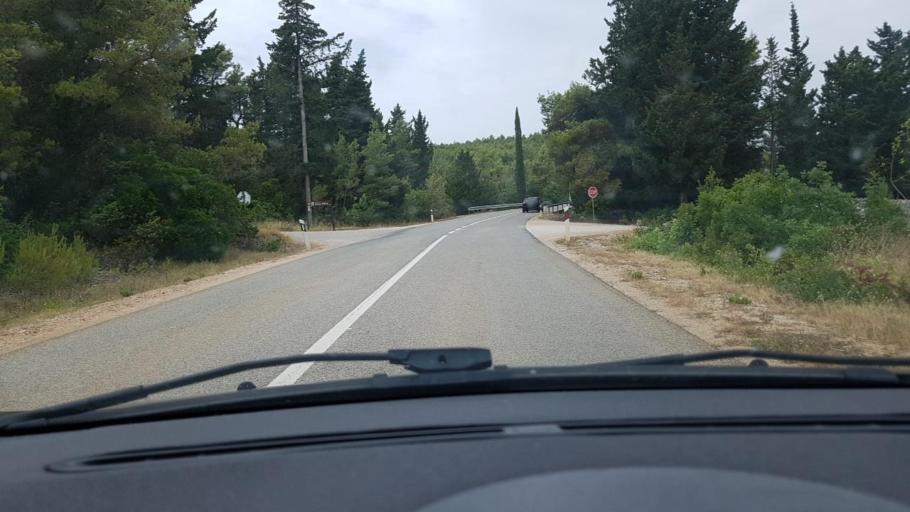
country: HR
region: Dubrovacko-Neretvanska
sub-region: Grad Korcula
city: Zrnovo
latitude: 42.9367
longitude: 17.0818
